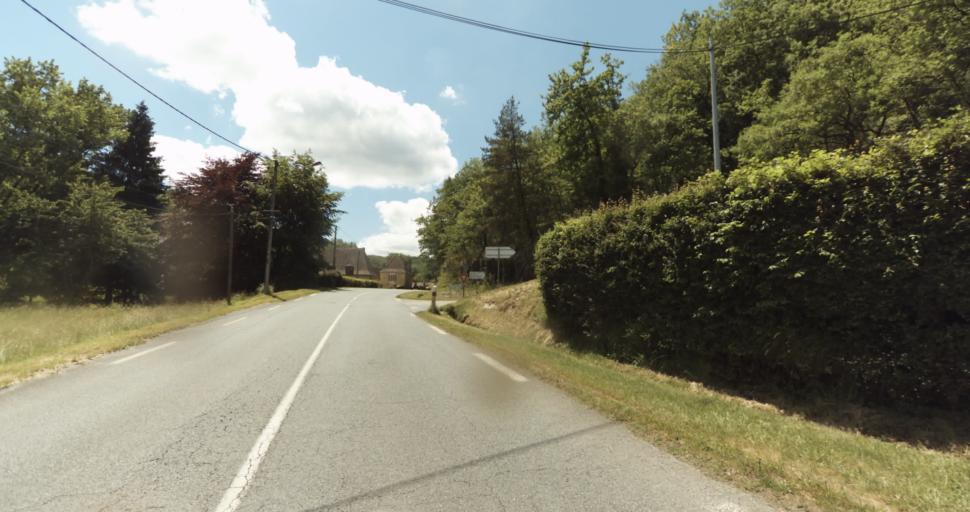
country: FR
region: Aquitaine
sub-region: Departement de la Dordogne
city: Le Bugue
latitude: 44.8455
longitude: 0.8963
